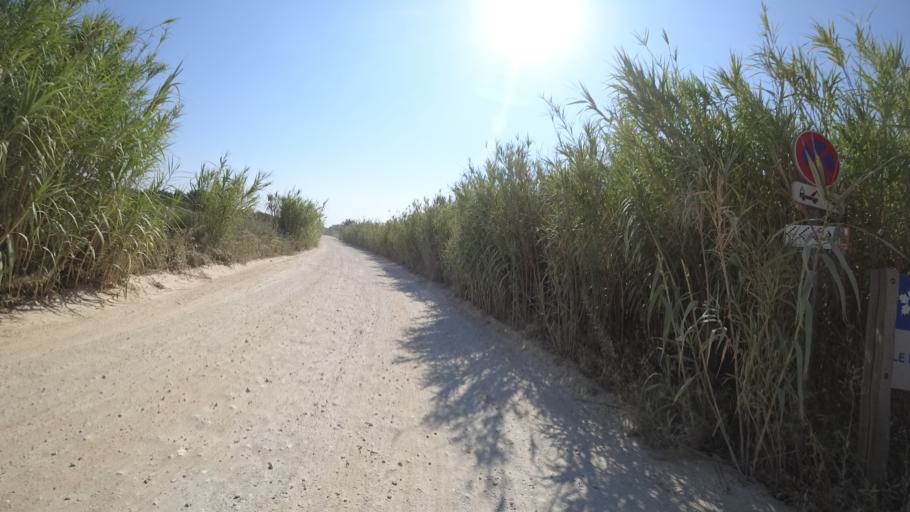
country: FR
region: Languedoc-Roussillon
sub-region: Departement des Pyrenees-Orientales
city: Le Barcares
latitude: 42.7566
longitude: 3.0285
